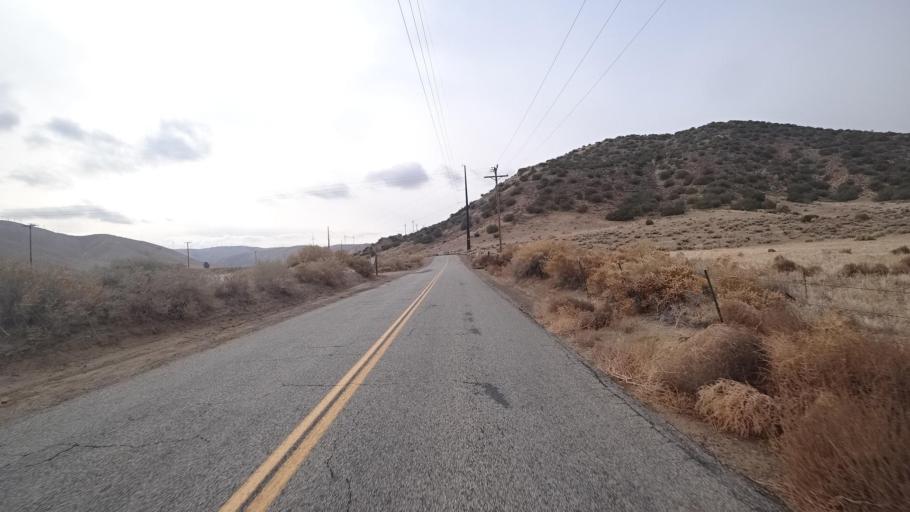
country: US
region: California
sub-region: Kern County
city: Tehachapi
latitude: 35.1314
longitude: -118.3253
